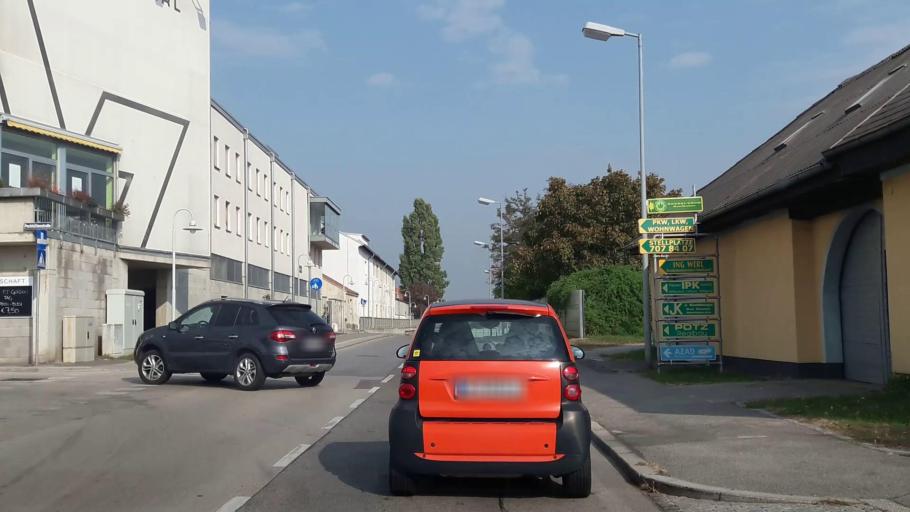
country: AT
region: Lower Austria
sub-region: Politischer Bezirk Wien-Umgebung
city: Schwechat
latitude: 48.1457
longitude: 16.4702
